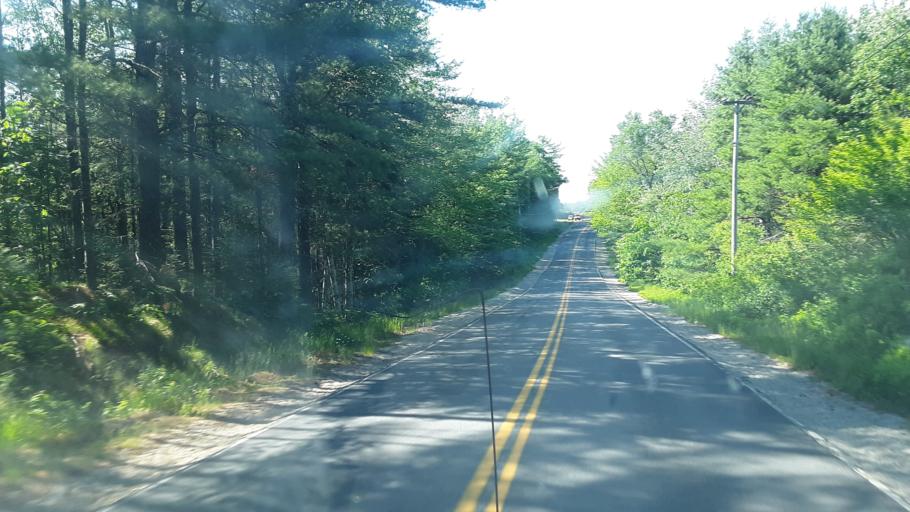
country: US
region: Maine
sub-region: Washington County
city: Cherryfield
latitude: 44.7580
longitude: -68.0249
